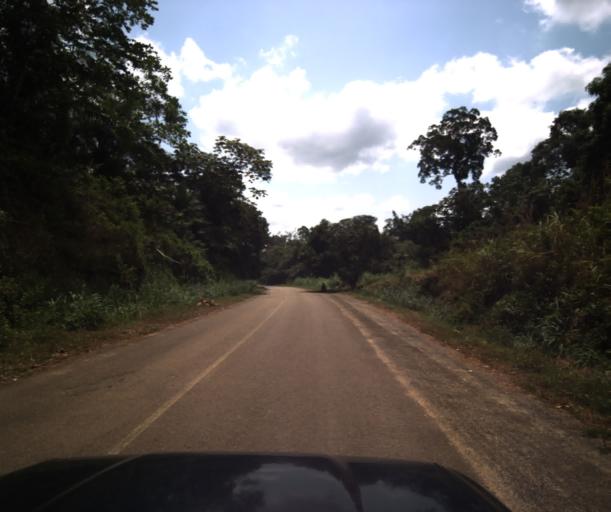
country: CM
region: Centre
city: Eseka
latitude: 3.8074
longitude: 10.8066
